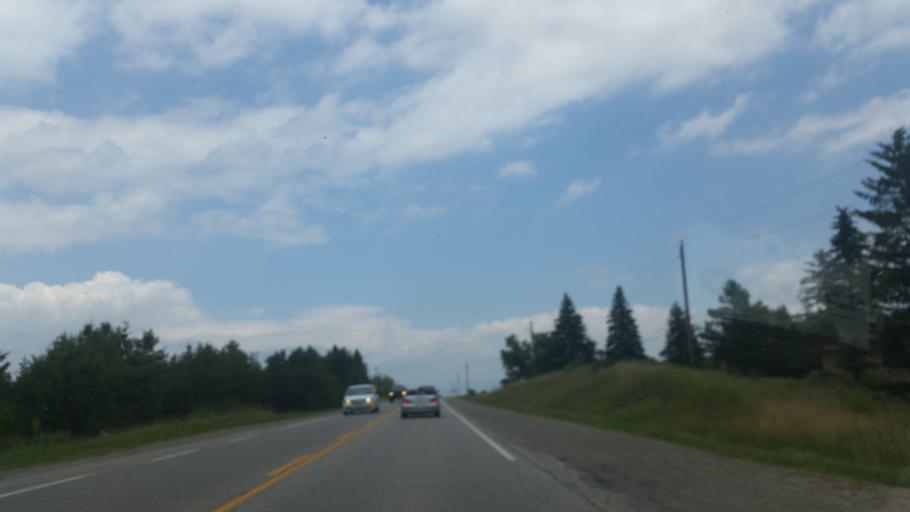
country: CA
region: Ontario
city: Orangeville
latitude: 43.7357
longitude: -80.0884
